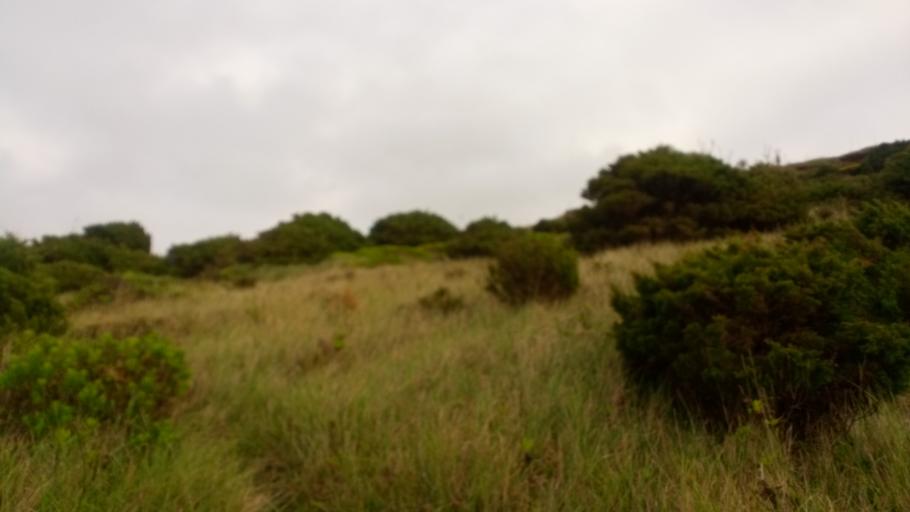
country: PT
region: Leiria
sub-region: Caldas da Rainha
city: Caldas da Rainha
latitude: 39.4907
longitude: -9.1793
